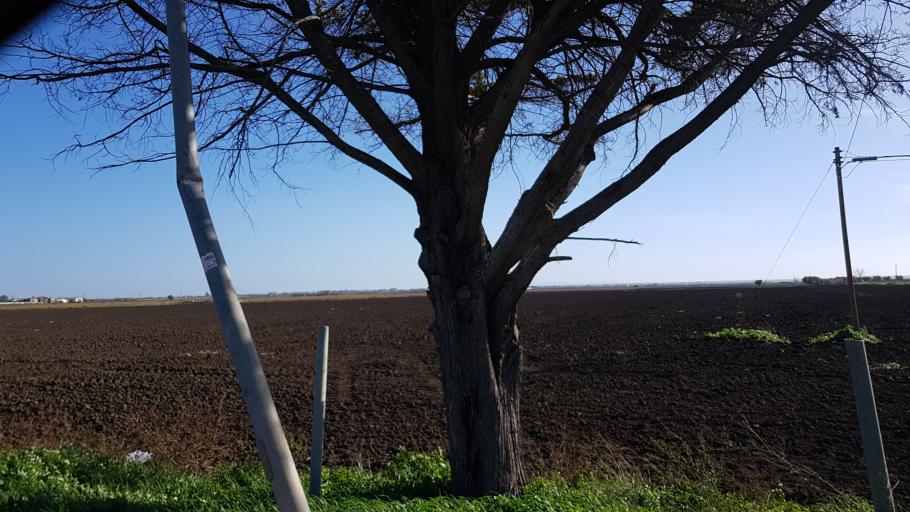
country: IT
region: Apulia
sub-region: Provincia di Foggia
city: Carapelle
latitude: 41.3816
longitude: 15.6440
